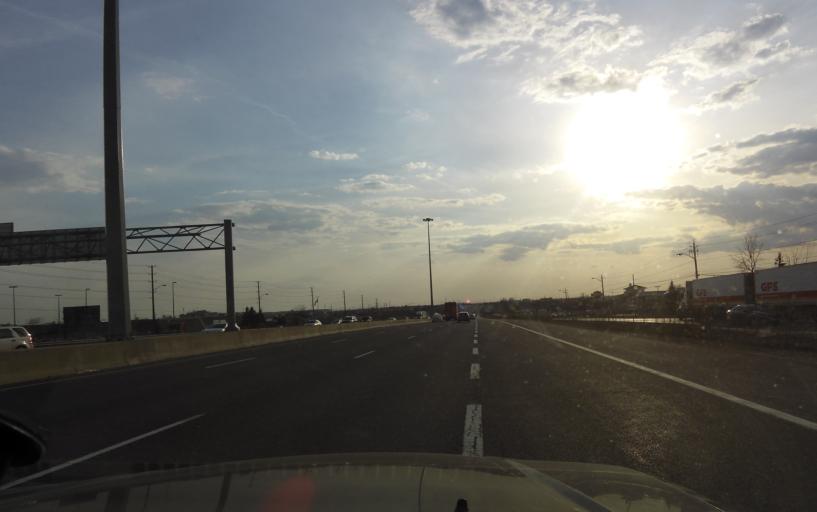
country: CA
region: Ontario
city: Oshawa
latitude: 43.8736
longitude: -78.8866
